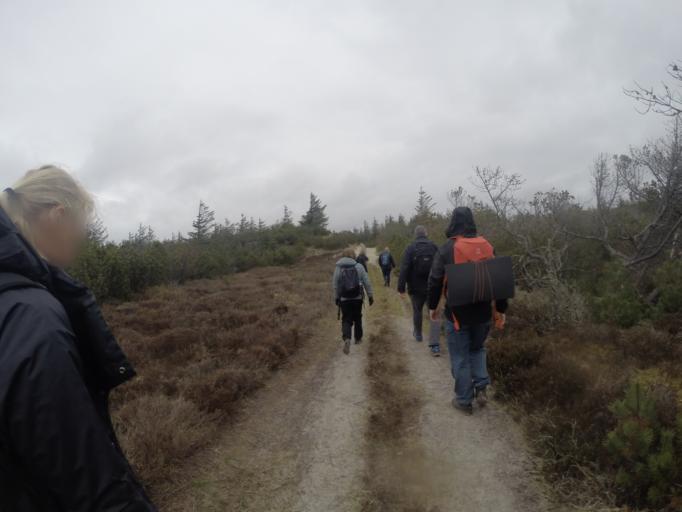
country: DK
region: North Denmark
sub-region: Thisted Kommune
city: Hurup
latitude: 56.8994
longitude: 8.3379
